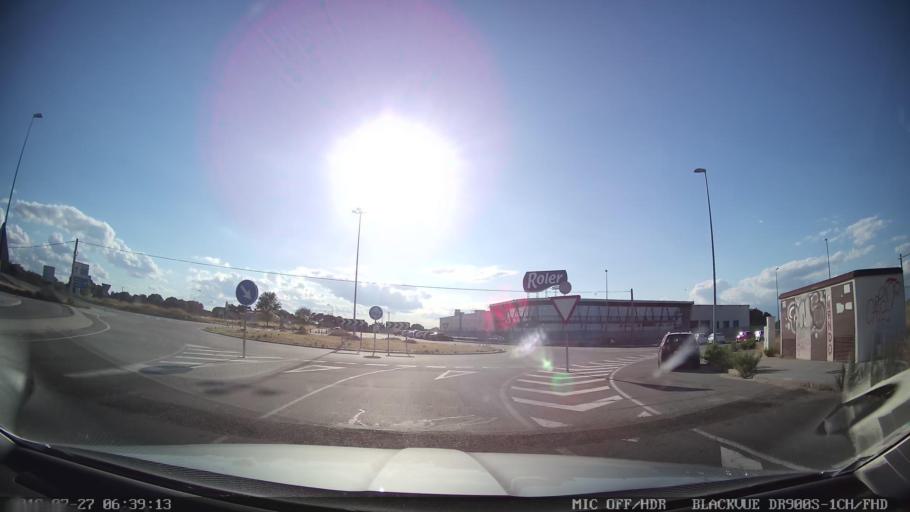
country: ES
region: Extremadura
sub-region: Provincia de Caceres
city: Peraleda de la Mata
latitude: 39.8927
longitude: -5.4287
